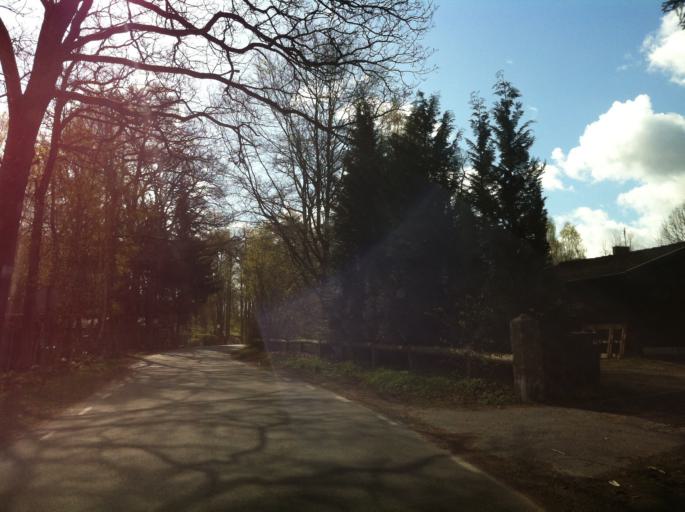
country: SE
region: Skane
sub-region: Hoors Kommun
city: Hoeoer
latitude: 55.9102
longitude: 13.4903
